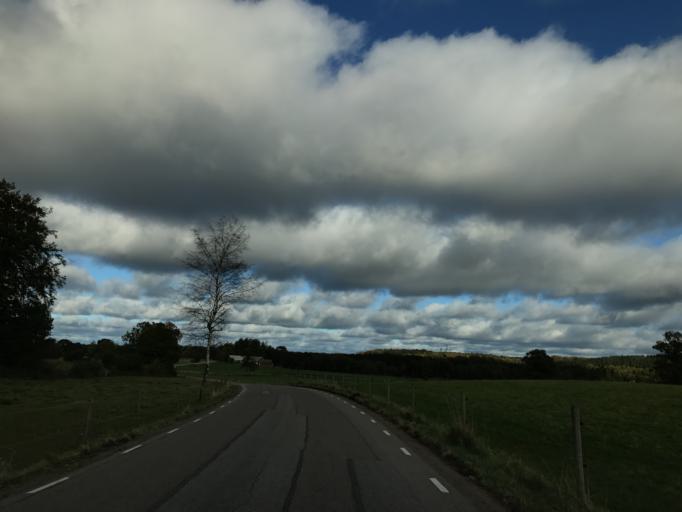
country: SE
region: Skane
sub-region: Svalovs Kommun
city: Kagerod
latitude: 56.0584
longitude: 13.1106
